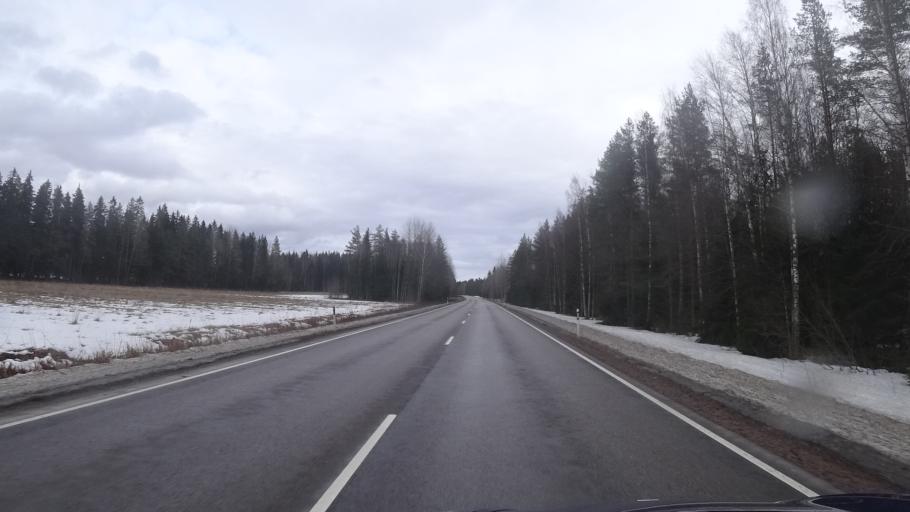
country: FI
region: Kymenlaakso
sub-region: Kouvola
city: Elimaeki
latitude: 60.6902
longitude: 26.6152
